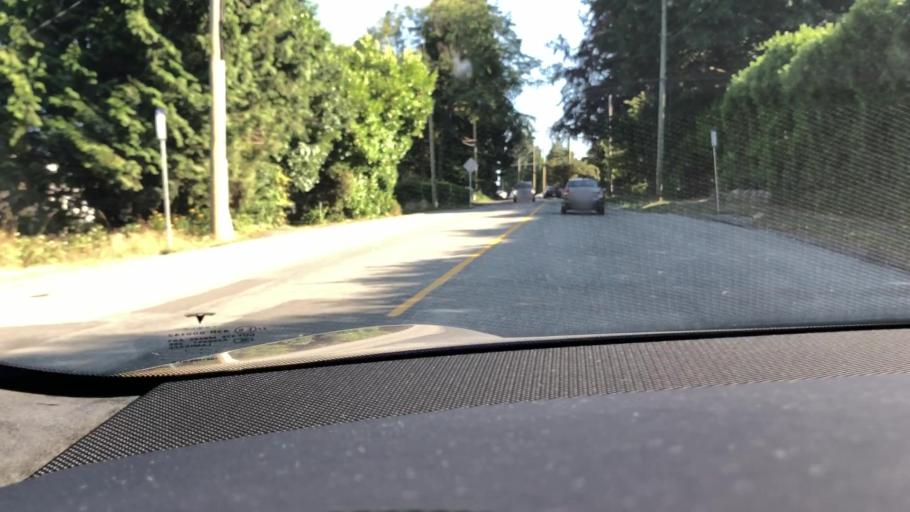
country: CA
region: British Columbia
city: Burnaby
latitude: 49.2534
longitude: -122.9820
